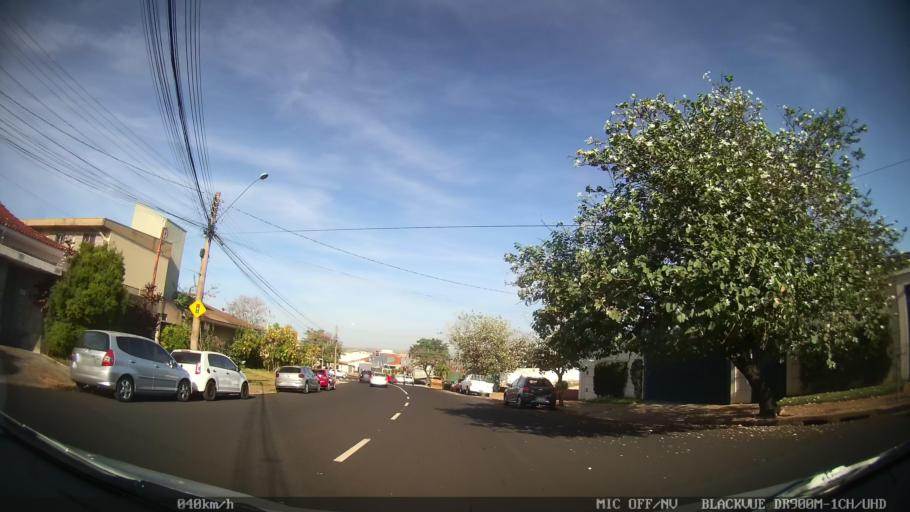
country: BR
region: Sao Paulo
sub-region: Ribeirao Preto
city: Ribeirao Preto
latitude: -21.1975
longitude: -47.8174
